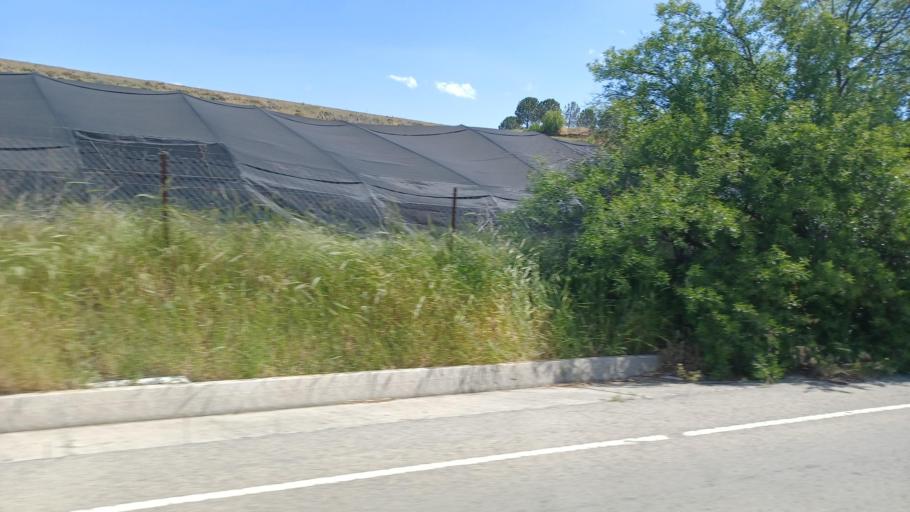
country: CY
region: Lefkosia
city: Astromeritis
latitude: 35.0600
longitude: 33.0264
